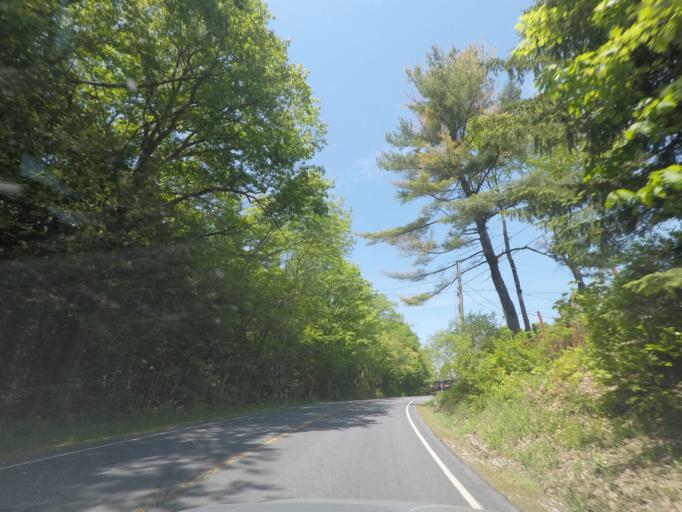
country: US
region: New York
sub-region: Rensselaer County
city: West Sand Lake
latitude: 42.6024
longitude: -73.6038
